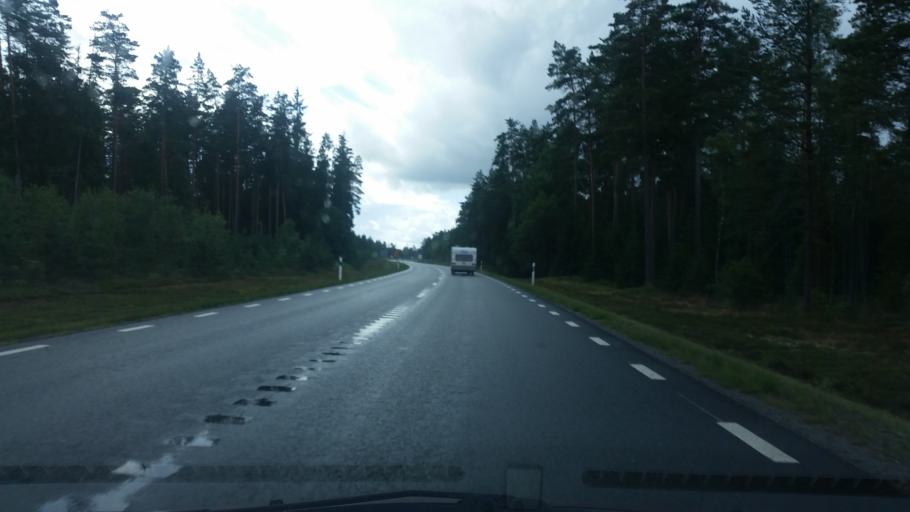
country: SE
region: Joenkoeping
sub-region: Gislaveds Kommun
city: Gislaved
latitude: 57.3547
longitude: 13.5584
